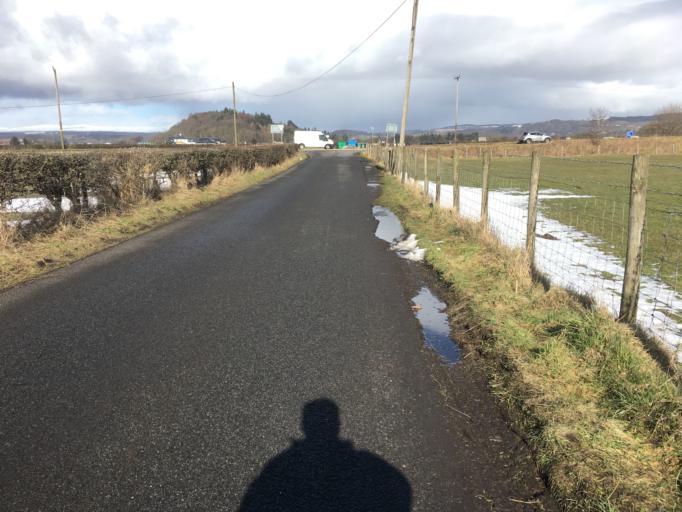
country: GB
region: Scotland
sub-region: Stirling
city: Stirling
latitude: 56.1181
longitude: -3.9740
